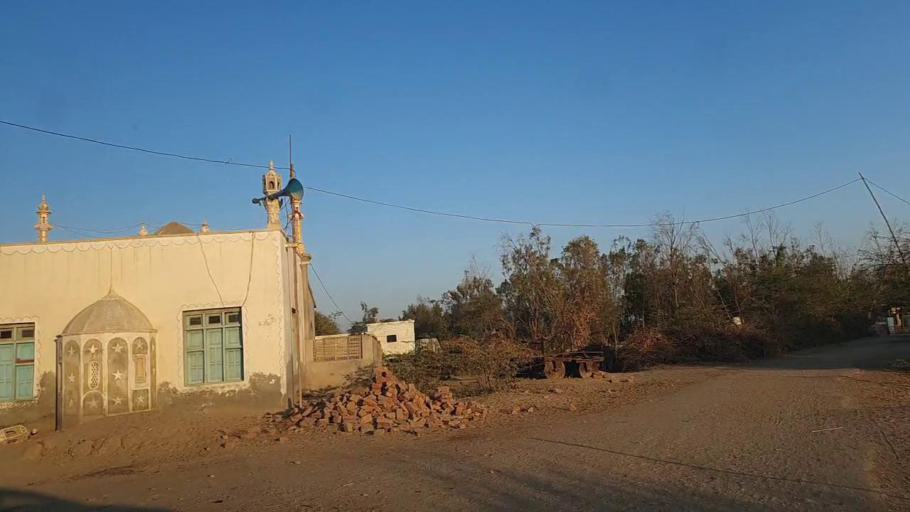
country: PK
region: Sindh
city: Naukot
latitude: 25.0329
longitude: 69.4266
